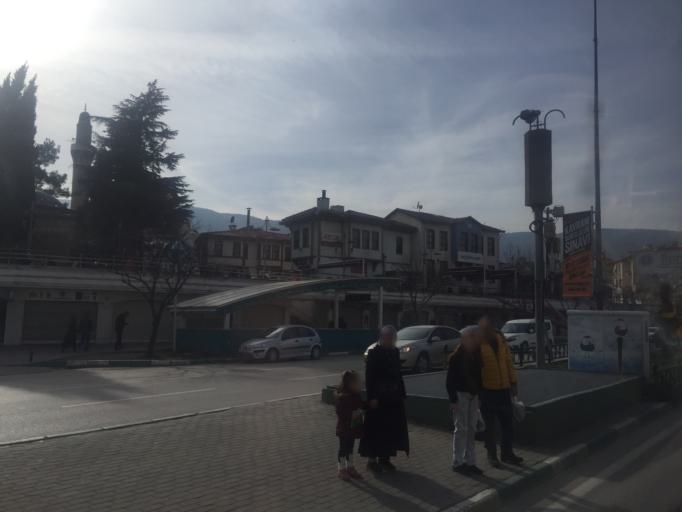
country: TR
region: Bursa
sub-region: Osmangazi
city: Bursa
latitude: 40.1874
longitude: 29.0686
